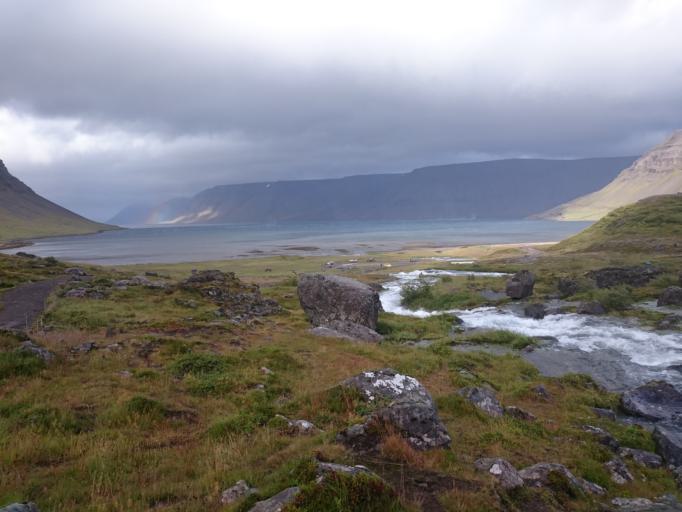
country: IS
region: Westfjords
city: Isafjoerdur
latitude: 65.7352
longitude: -23.2048
